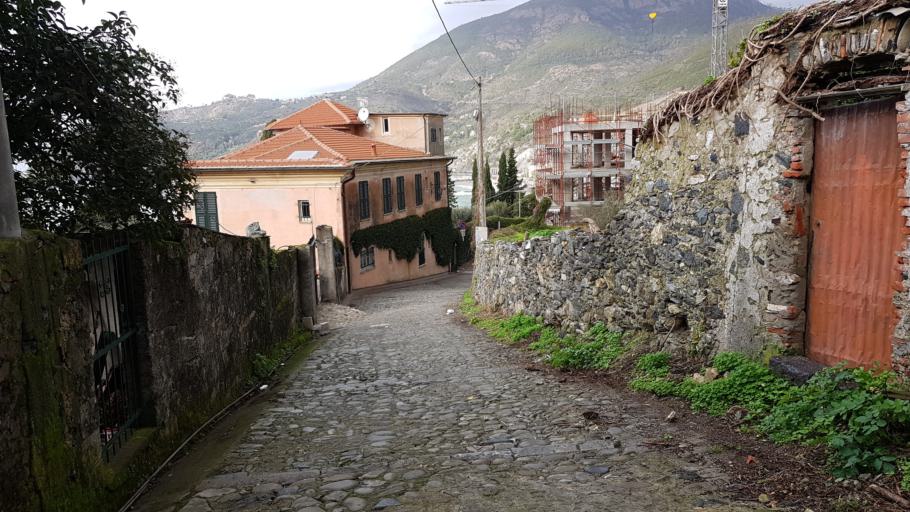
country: IT
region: Liguria
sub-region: Provincia di La Spezia
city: Levanto
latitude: 44.1655
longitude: 9.6111
